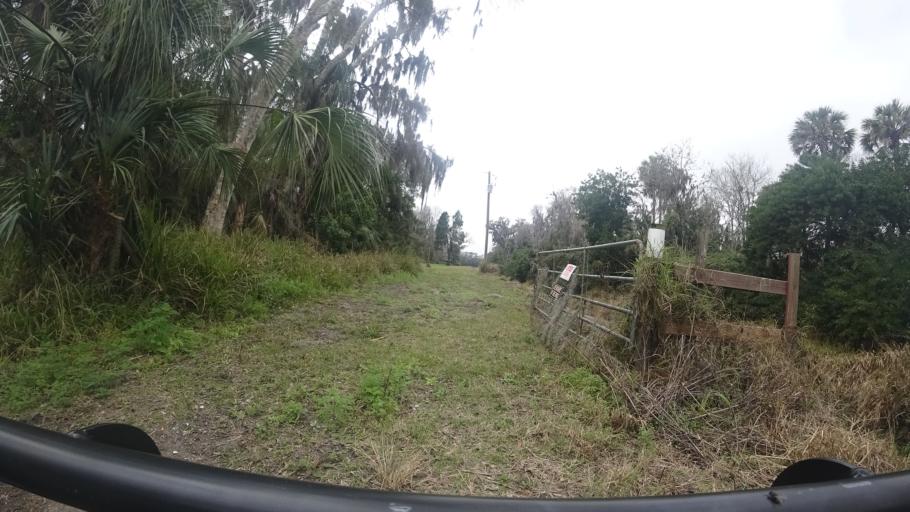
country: US
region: Florida
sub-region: Manatee County
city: Ellenton
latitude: 27.5808
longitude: -82.5030
